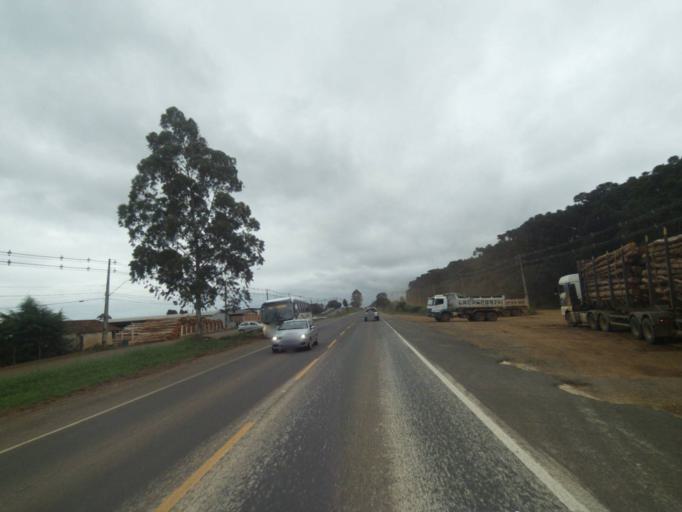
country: BR
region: Parana
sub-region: Telemaco Borba
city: Telemaco Borba
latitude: -24.3631
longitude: -50.6584
